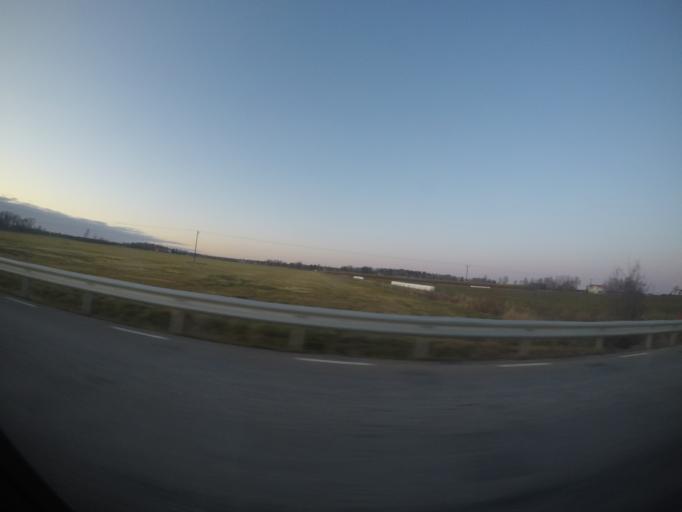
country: SE
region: OErebro
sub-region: Orebro Kommun
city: Hovsta
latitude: 59.3141
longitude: 15.3288
